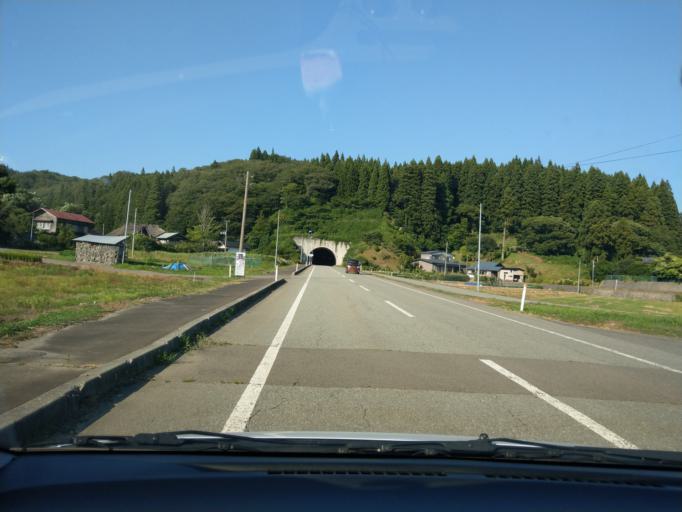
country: JP
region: Akita
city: Akita
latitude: 39.6015
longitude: 140.2178
